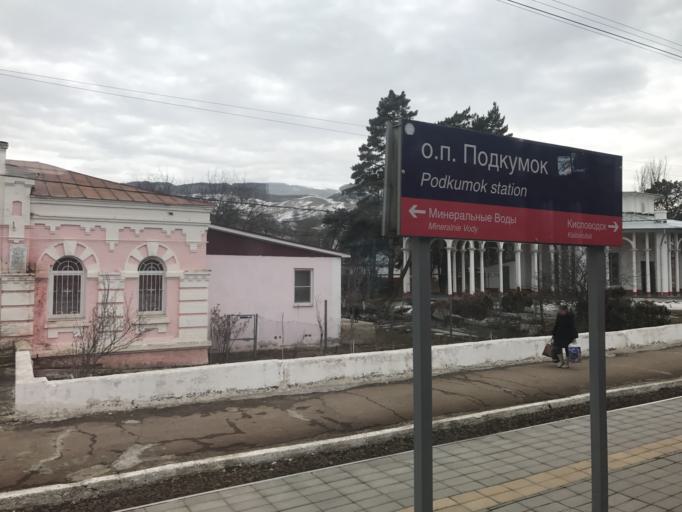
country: RU
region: Stavropol'skiy
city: Yasnaya Polyana
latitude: 43.9615
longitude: 42.7712
